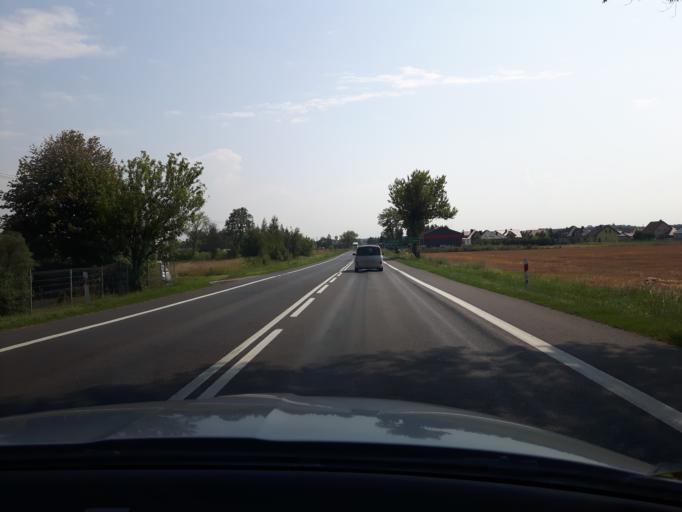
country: PL
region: Masovian Voivodeship
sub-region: Powiat mlawski
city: Strzegowo
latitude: 52.9024
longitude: 20.2869
